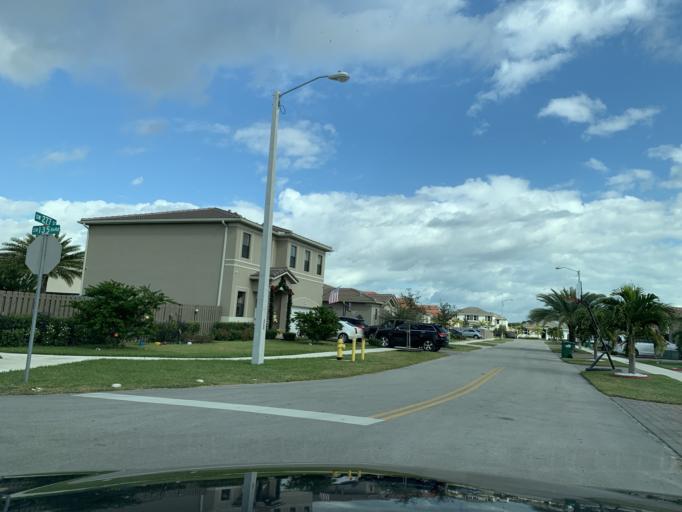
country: US
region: Florida
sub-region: Miami-Dade County
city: Naranja
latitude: 25.5100
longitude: -80.4104
